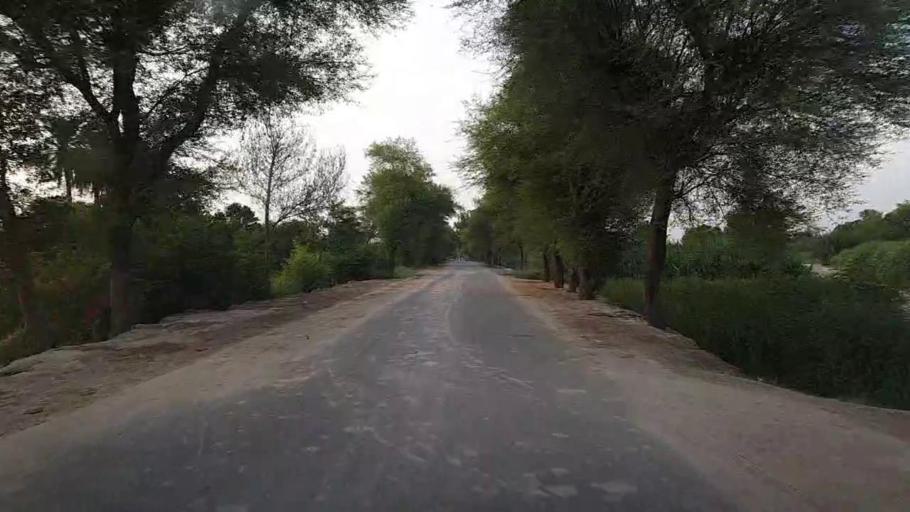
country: PK
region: Sindh
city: Ubauro
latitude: 28.2870
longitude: 69.8002
